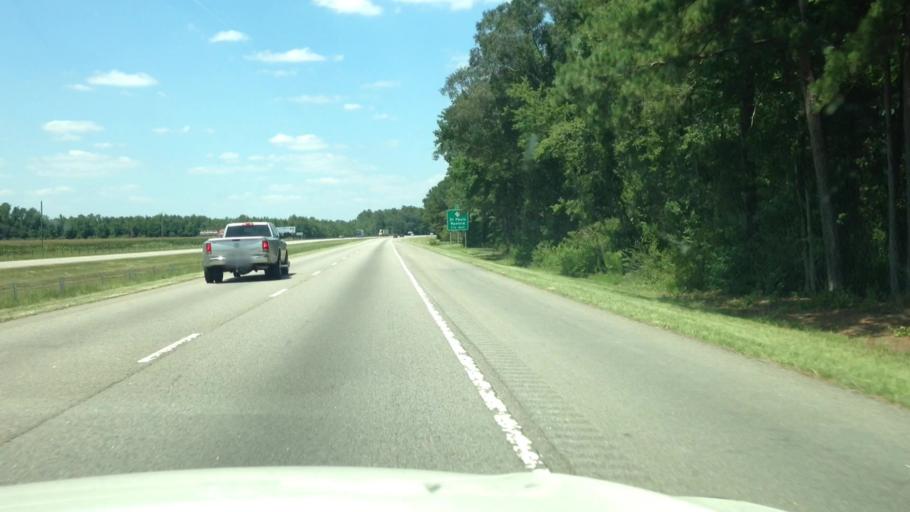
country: US
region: North Carolina
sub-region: Robeson County
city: Saint Pauls
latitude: 34.7882
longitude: -78.9944
